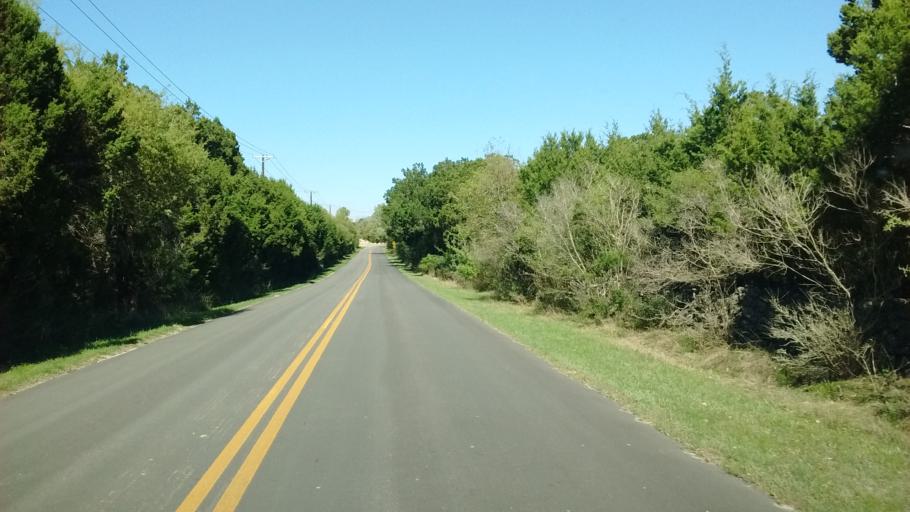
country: US
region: Texas
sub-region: Comal County
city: New Braunfels
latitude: 29.7218
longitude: -98.2022
